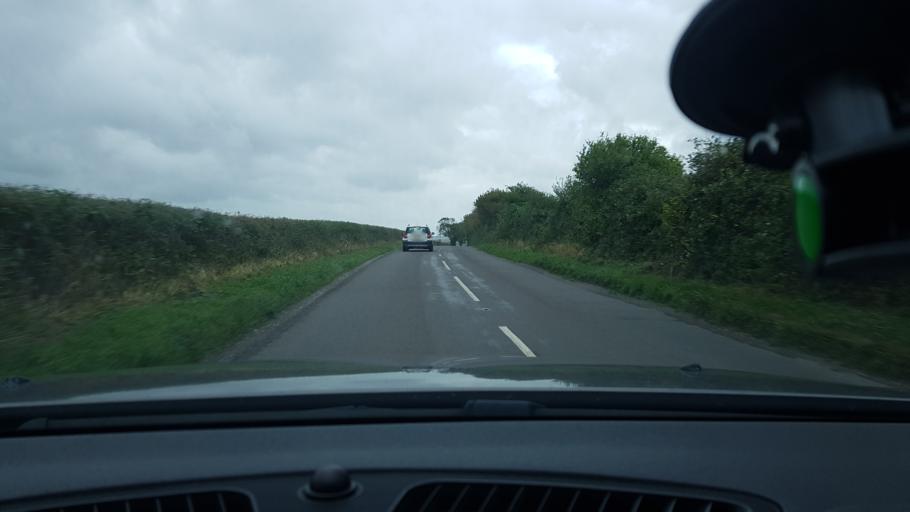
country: GB
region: England
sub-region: Wiltshire
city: Great Bedwyn
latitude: 51.3505
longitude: -1.5838
